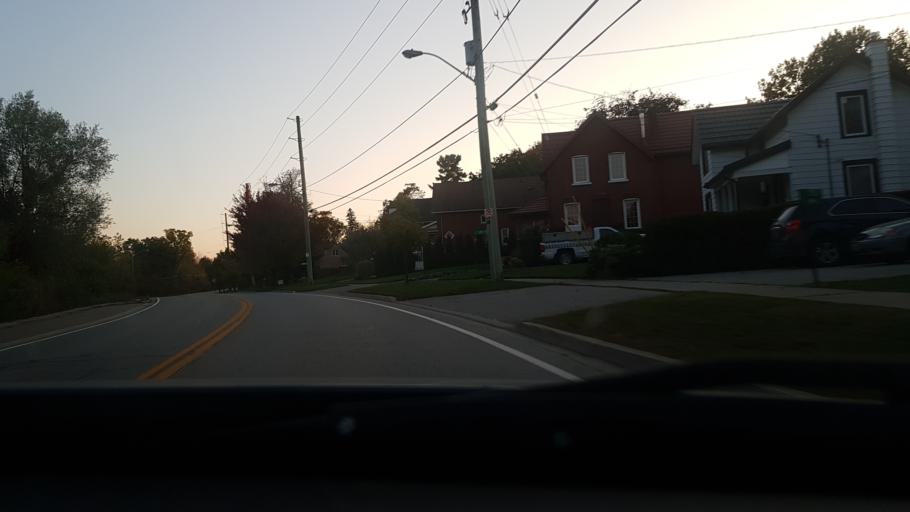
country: CA
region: Ontario
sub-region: Halton
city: Milton
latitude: 43.4857
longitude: -79.9835
